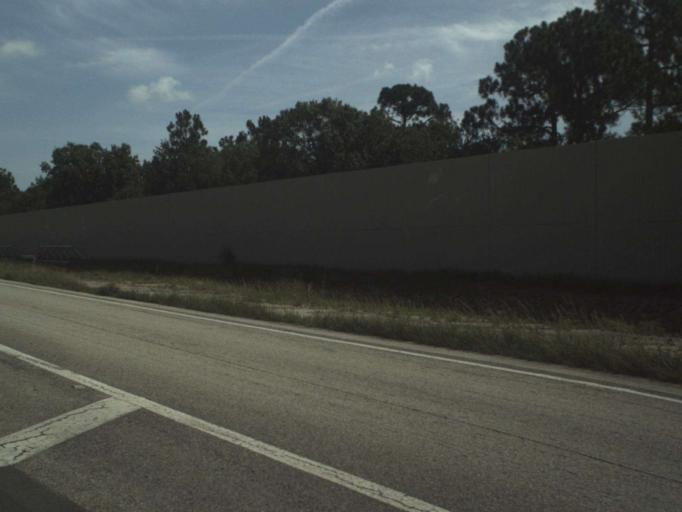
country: US
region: Florida
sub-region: Indian River County
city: Fellsmere
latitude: 27.7641
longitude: -80.5511
